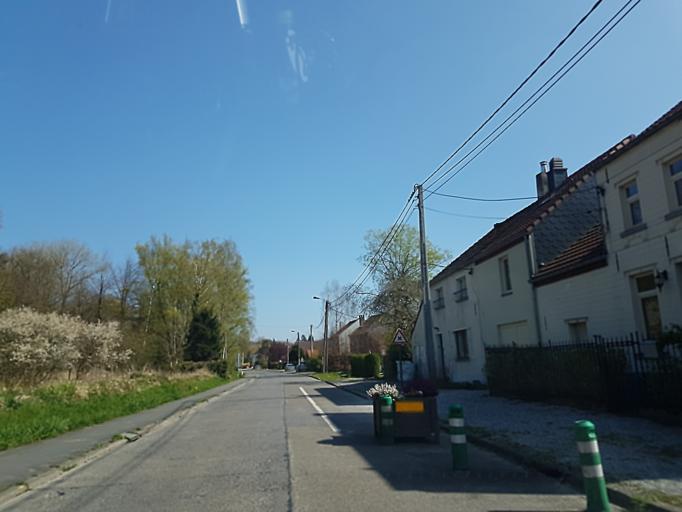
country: BE
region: Flanders
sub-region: Provincie Vlaams-Brabant
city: Oud-Heverlee
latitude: 50.7914
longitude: 4.6640
